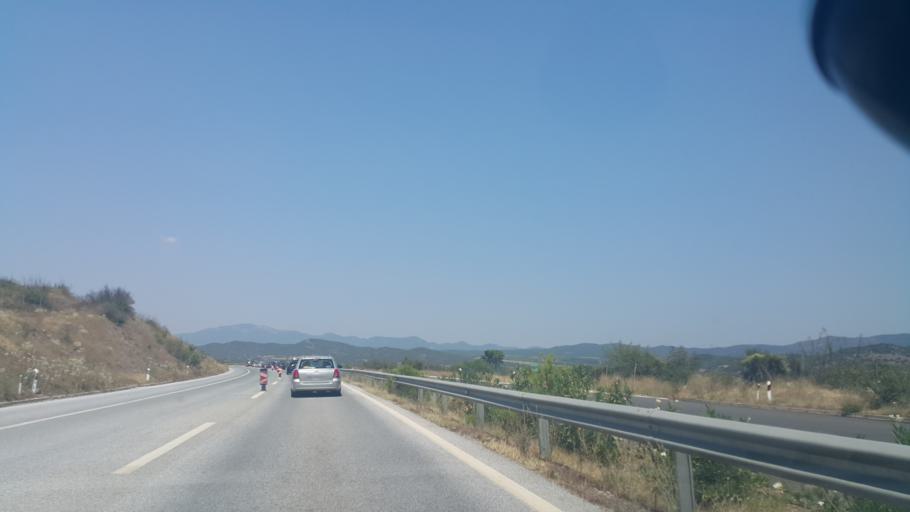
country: MK
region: Bogdanci
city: Bogdanci
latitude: 41.2292
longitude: 22.4921
